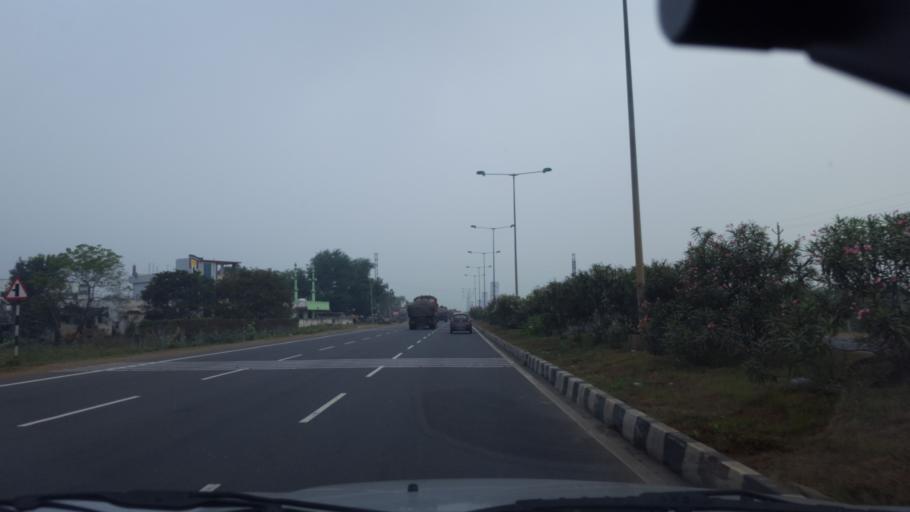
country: IN
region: Andhra Pradesh
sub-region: Prakasam
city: Ongole
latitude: 15.6340
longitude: 80.0166
